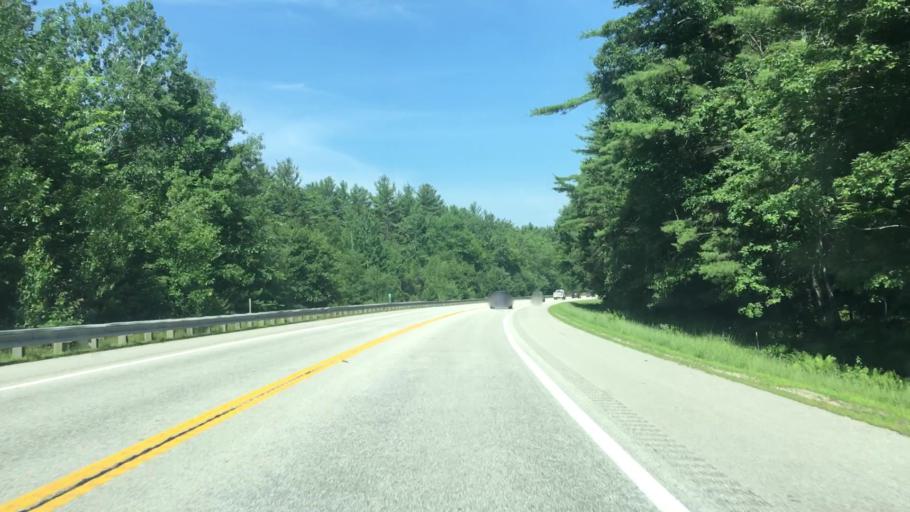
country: US
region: New Hampshire
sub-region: Merrimack County
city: Henniker
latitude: 43.1853
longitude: -71.7998
